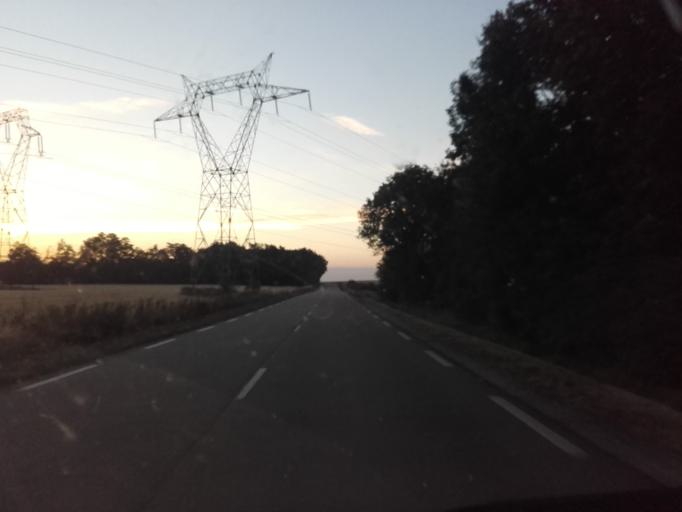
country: FR
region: Bourgogne
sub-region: Departement de l'Yonne
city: Tonnerre
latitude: 47.8175
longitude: 3.9060
